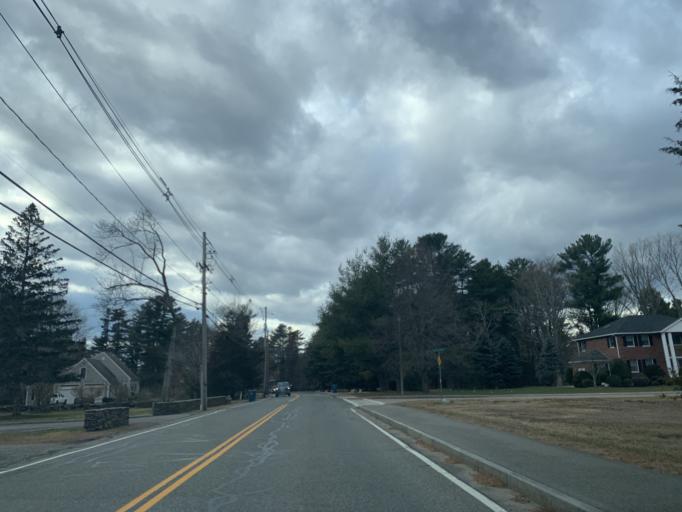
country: US
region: Massachusetts
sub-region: Norfolk County
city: Canton
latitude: 42.1704
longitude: -71.1454
